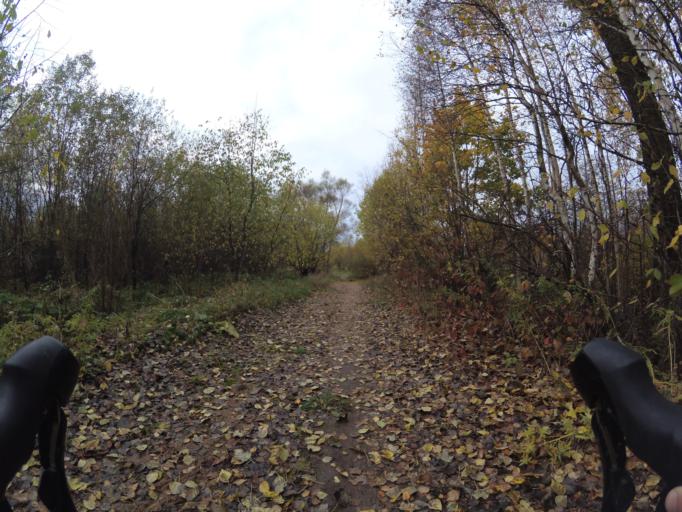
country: RU
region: St.-Petersburg
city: Lakhtinskiy
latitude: 60.0065
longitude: 30.1457
